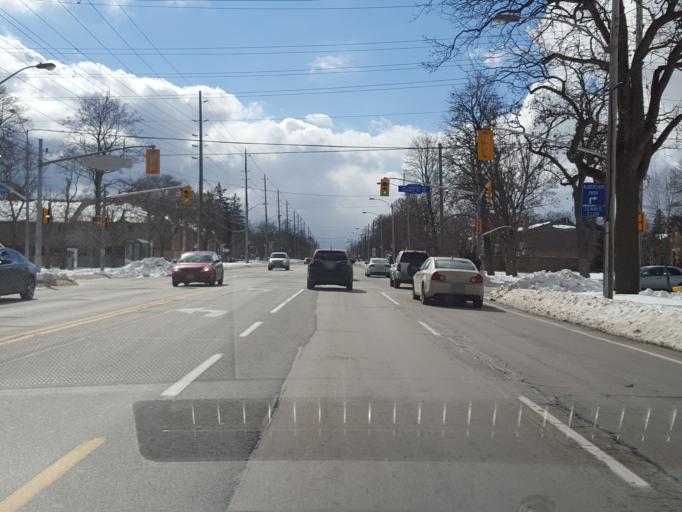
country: CA
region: Ontario
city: Hamilton
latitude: 43.3133
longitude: -79.8442
